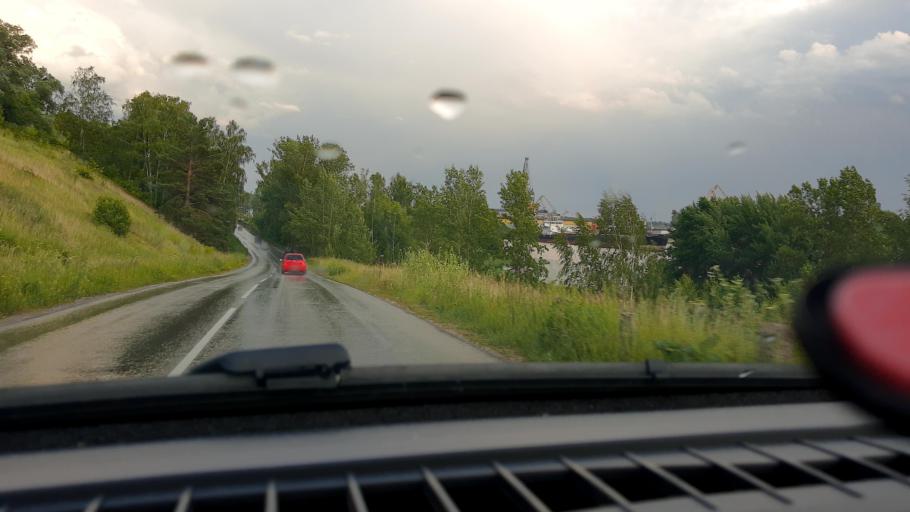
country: RU
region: Nizjnij Novgorod
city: Gorodets
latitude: 56.6842
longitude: 43.4292
